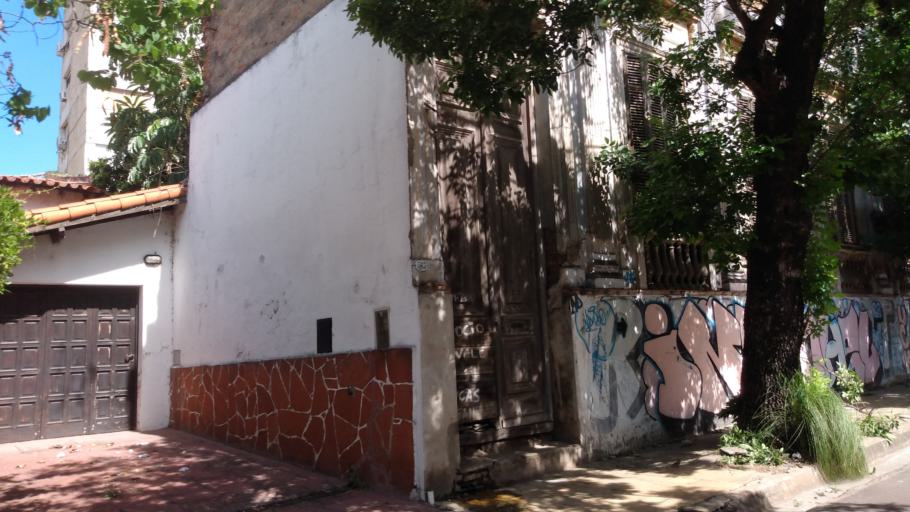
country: AR
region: Corrientes
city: Corrientes
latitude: -27.4632
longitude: -58.8413
